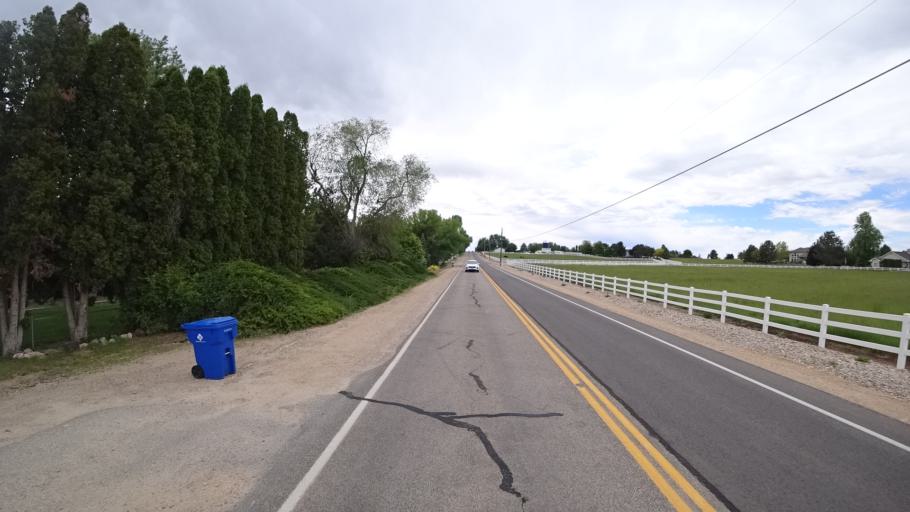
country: US
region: Idaho
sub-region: Ada County
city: Meridian
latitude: 43.5790
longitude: -116.4137
